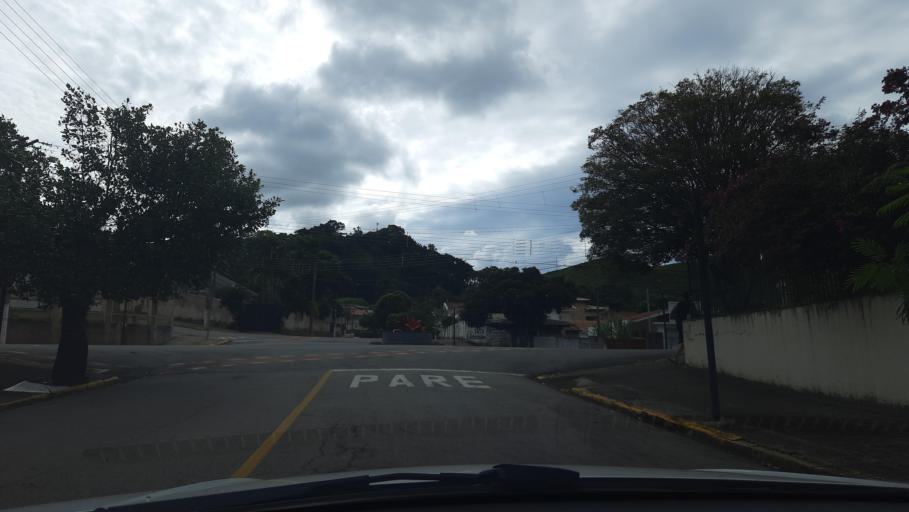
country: BR
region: Sao Paulo
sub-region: Sao Joao Da Boa Vista
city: Sao Joao da Boa Vista
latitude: -21.9393
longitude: -46.7178
